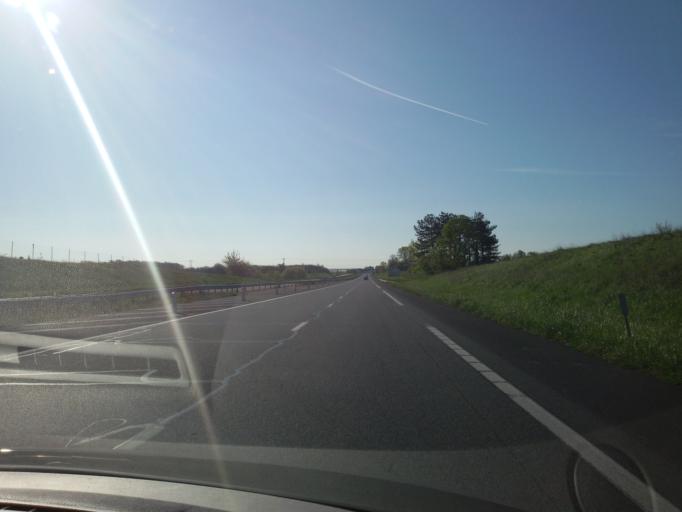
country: FR
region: Ile-de-France
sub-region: Departement de Seine-et-Marne
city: Souppes-sur-Loing
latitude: 48.2132
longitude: 2.7804
